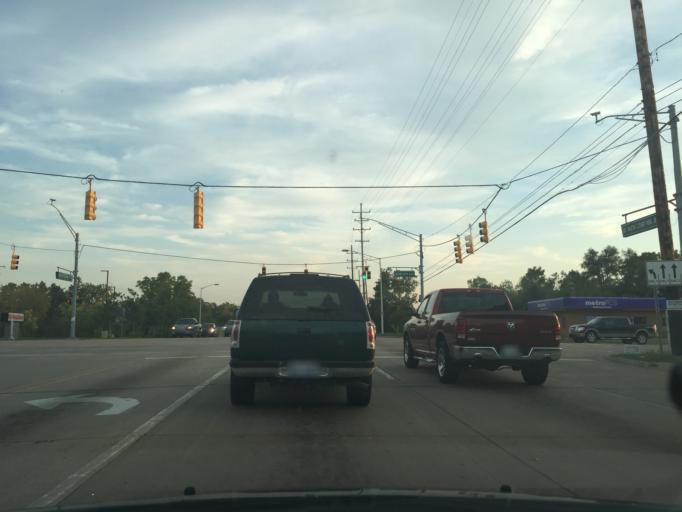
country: US
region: Michigan
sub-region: Oakland County
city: Pontiac
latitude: 42.6351
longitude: -83.2688
